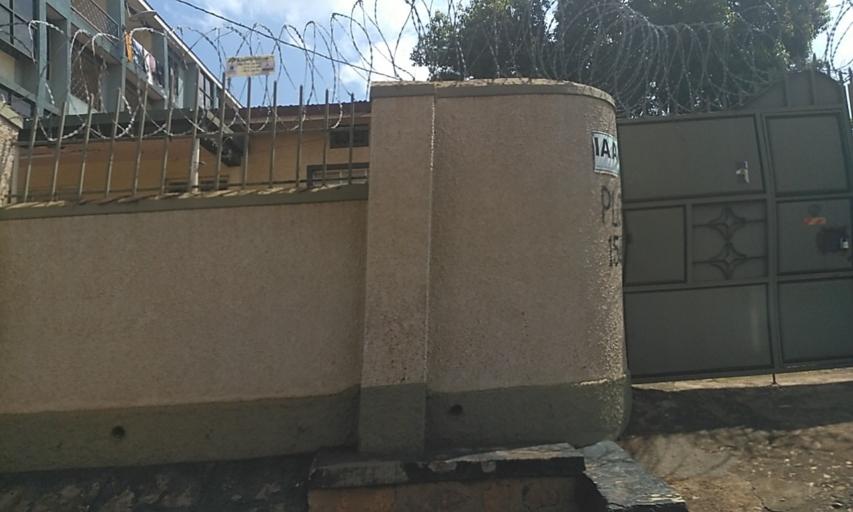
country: UG
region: Central Region
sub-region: Wakiso District
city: Kireka
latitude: 0.3457
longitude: 32.6167
